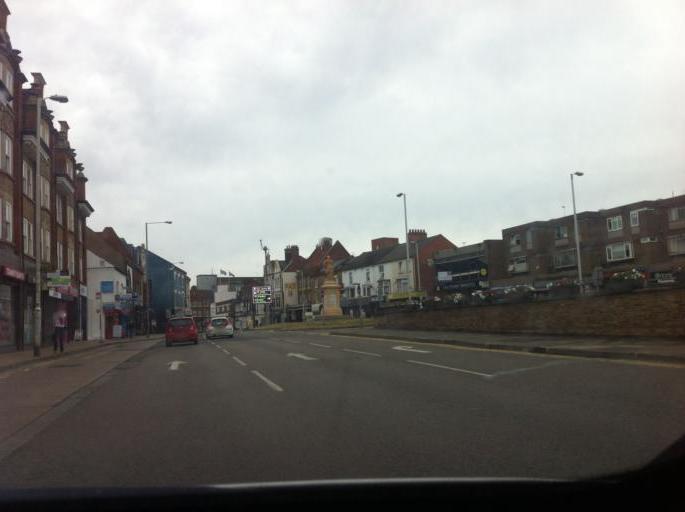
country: GB
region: England
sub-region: Northamptonshire
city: Northampton
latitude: 52.2404
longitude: -0.8867
